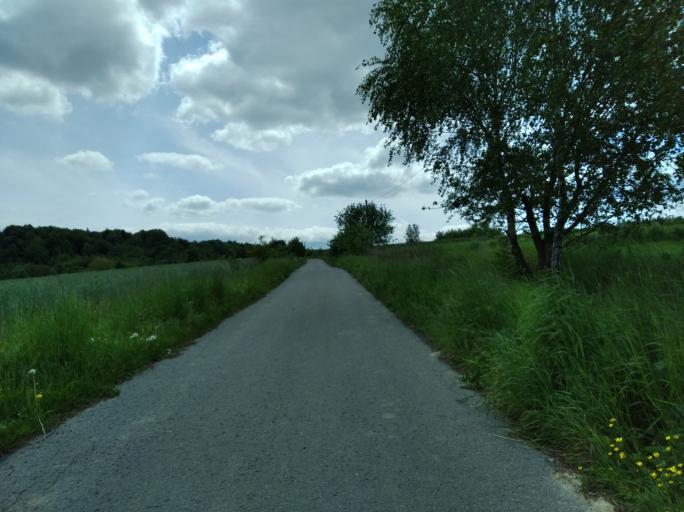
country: PL
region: Subcarpathian Voivodeship
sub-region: Powiat ropczycko-sedziszowski
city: Wielopole Skrzynskie
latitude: 49.9275
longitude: 21.6224
